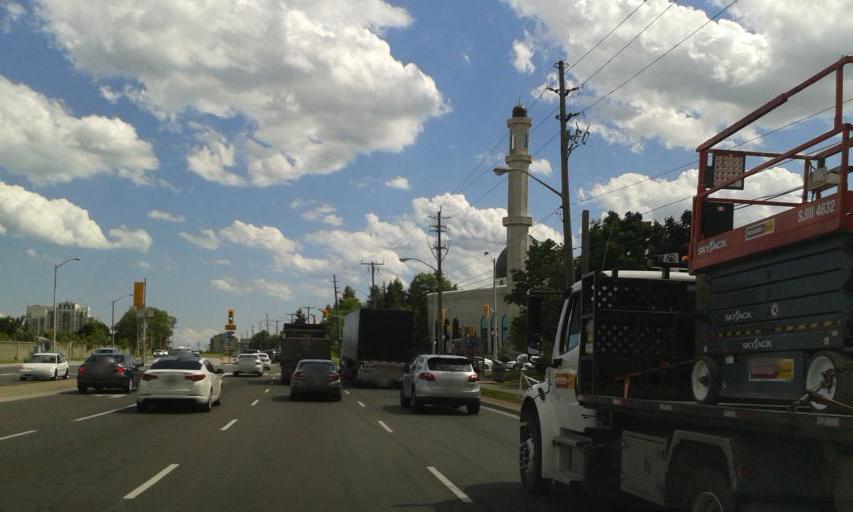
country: CA
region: Ontario
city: Scarborough
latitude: 43.7993
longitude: -79.2414
